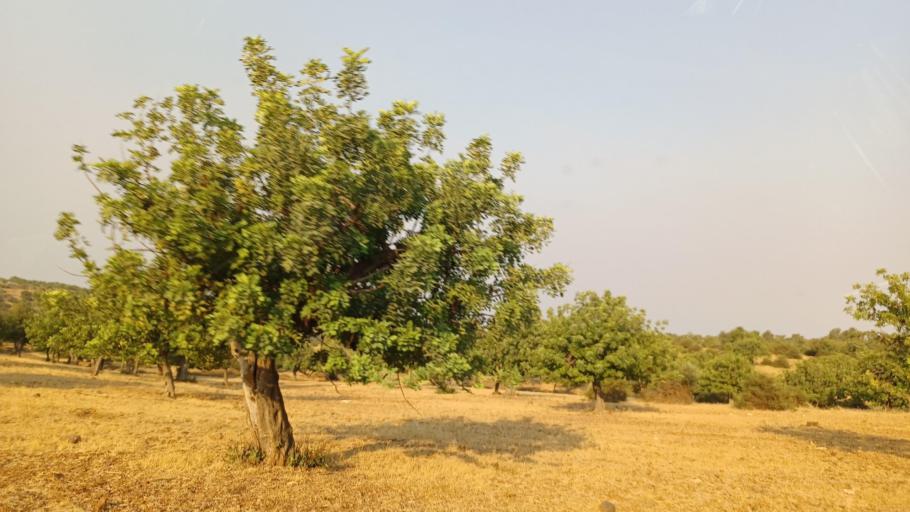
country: CY
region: Limassol
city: Pissouri
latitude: 34.6984
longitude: 32.6592
